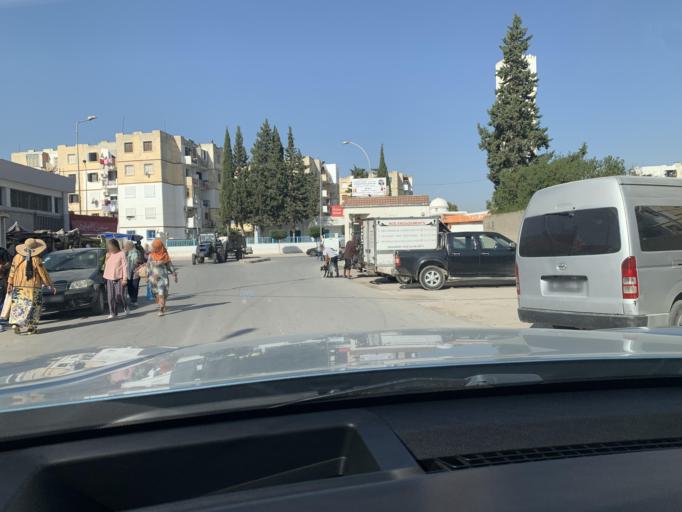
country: TN
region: Manouba
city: Manouba
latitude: 36.8227
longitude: 10.1194
